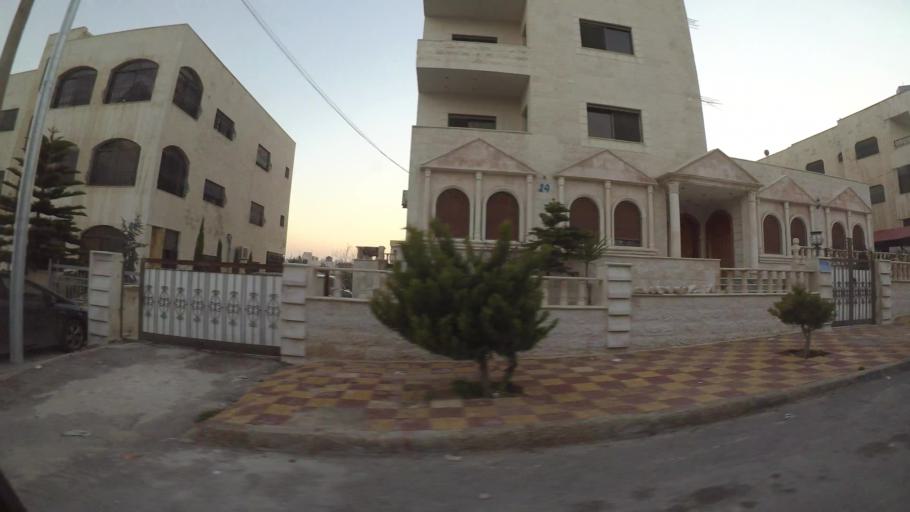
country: JO
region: Amman
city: Al Quwaysimah
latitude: 31.8938
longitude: 35.9264
